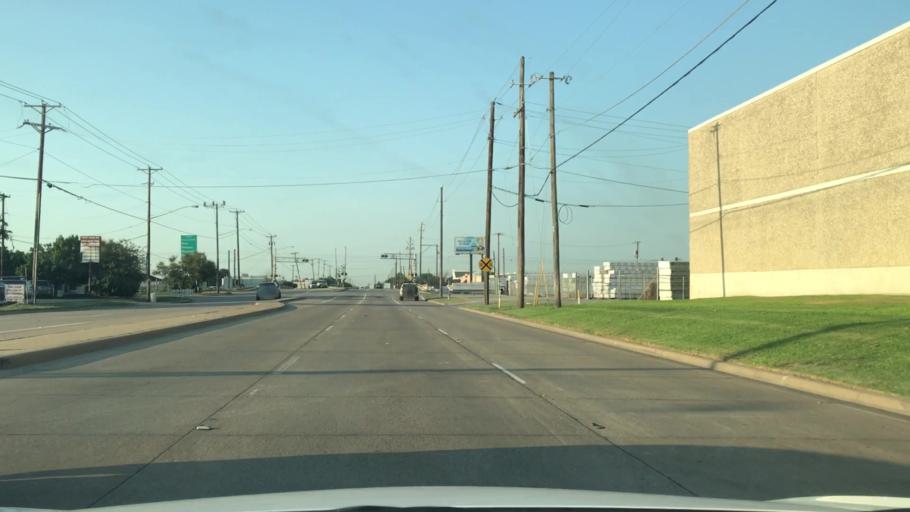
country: US
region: Texas
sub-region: Dallas County
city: Richardson
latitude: 32.9031
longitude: -96.7006
